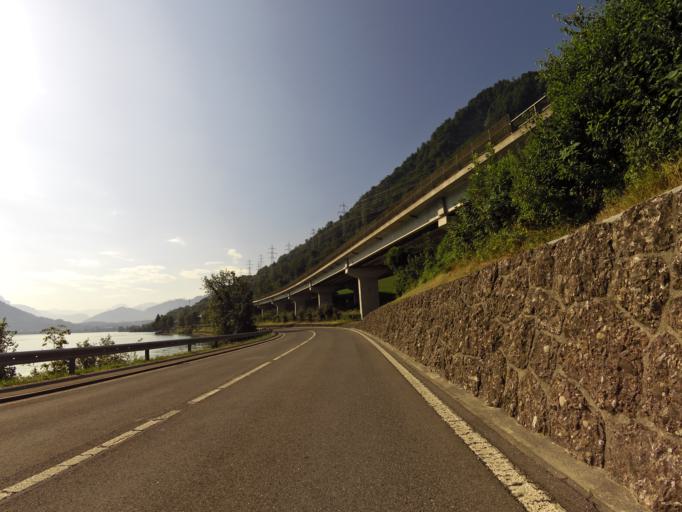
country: CH
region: Schwyz
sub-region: Bezirk Schwyz
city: Arth
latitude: 47.0771
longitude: 8.4892
